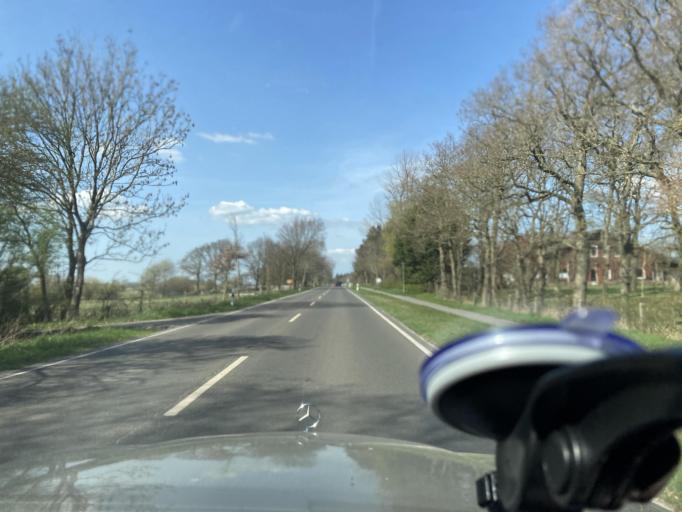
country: DE
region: Schleswig-Holstein
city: Stelle-Wittenwurth
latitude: 54.2838
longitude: 9.0448
